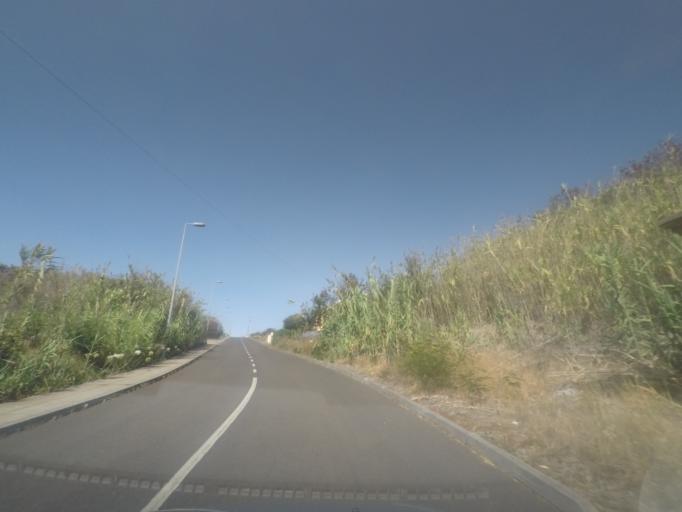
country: PT
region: Madeira
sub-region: Calheta
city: Faja da Ovelha
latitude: 32.8142
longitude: -17.2562
